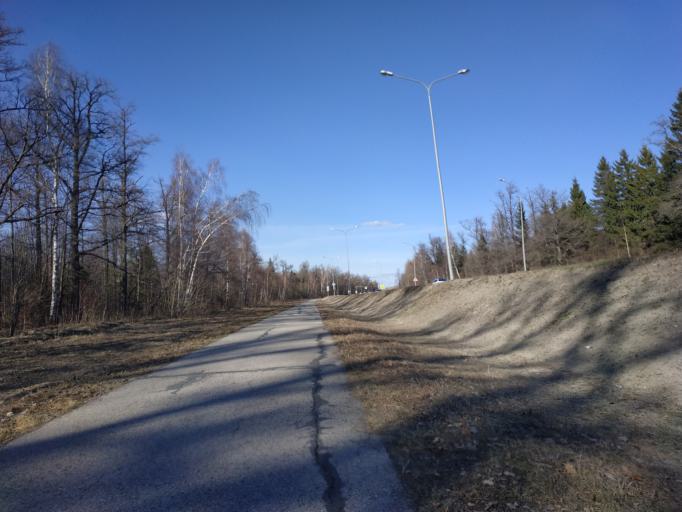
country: RU
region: Chuvashia
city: Ishley
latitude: 56.1243
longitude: 47.0623
